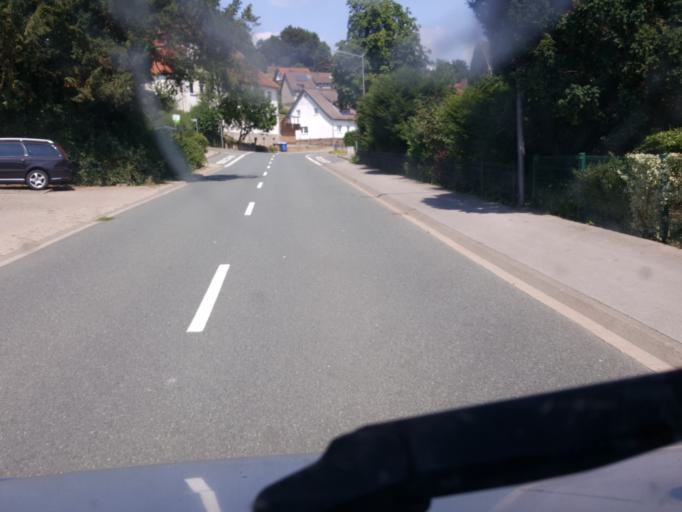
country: DE
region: North Rhine-Westphalia
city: Bad Oeynhausen
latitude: 52.2649
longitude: 8.7693
